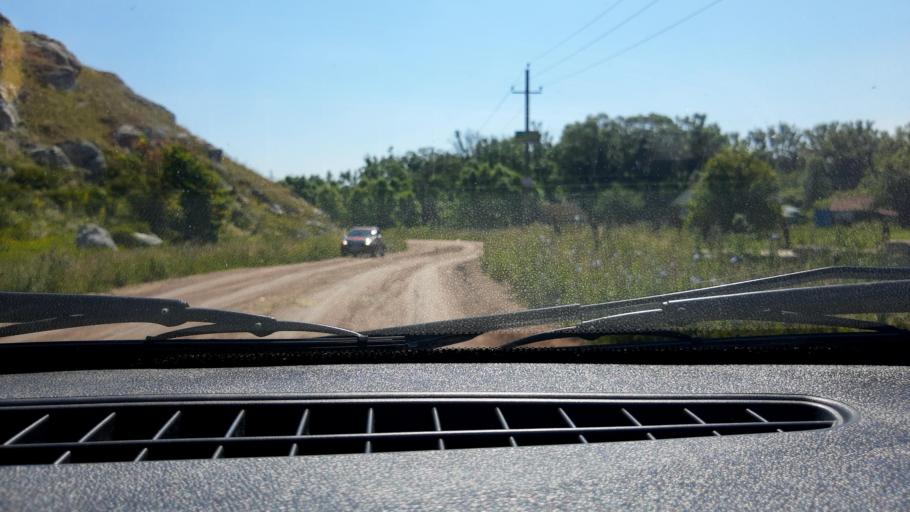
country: RU
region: Bashkortostan
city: Karmaskaly
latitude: 54.3597
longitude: 55.8988
